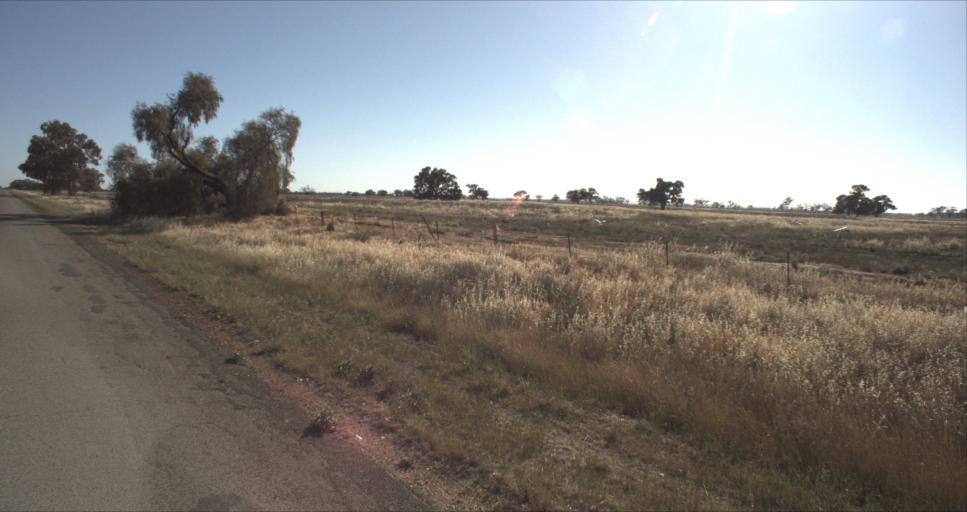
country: AU
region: New South Wales
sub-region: Leeton
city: Leeton
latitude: -34.6002
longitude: 146.2579
